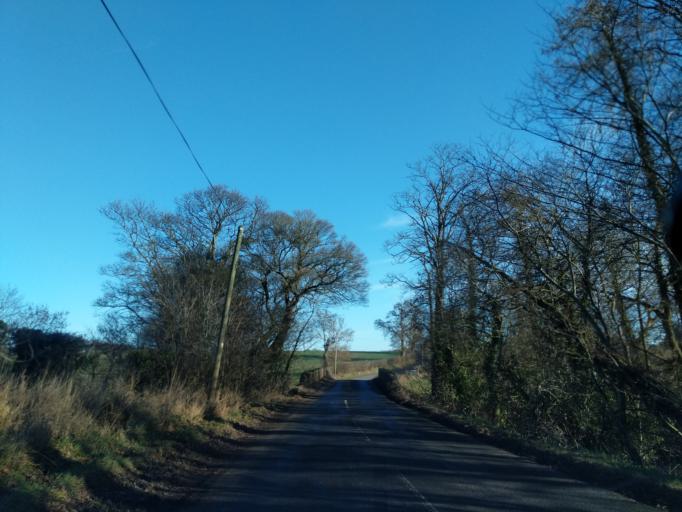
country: GB
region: Scotland
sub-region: East Lothian
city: Haddington
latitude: 55.9630
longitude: -2.7194
